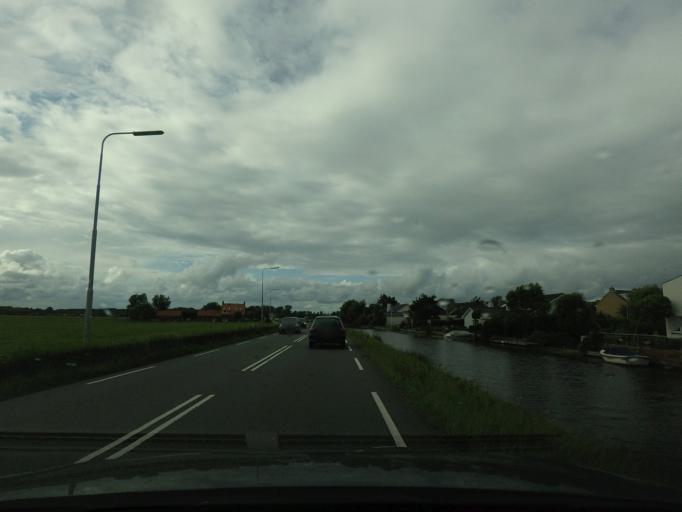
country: NL
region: South Holland
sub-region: Gemeente Teylingen
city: Voorhout
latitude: 52.2219
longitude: 4.4761
